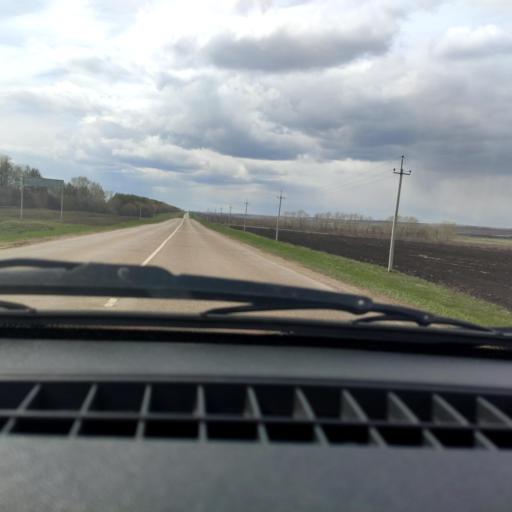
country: RU
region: Bashkortostan
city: Chekmagush
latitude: 55.1092
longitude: 54.9455
